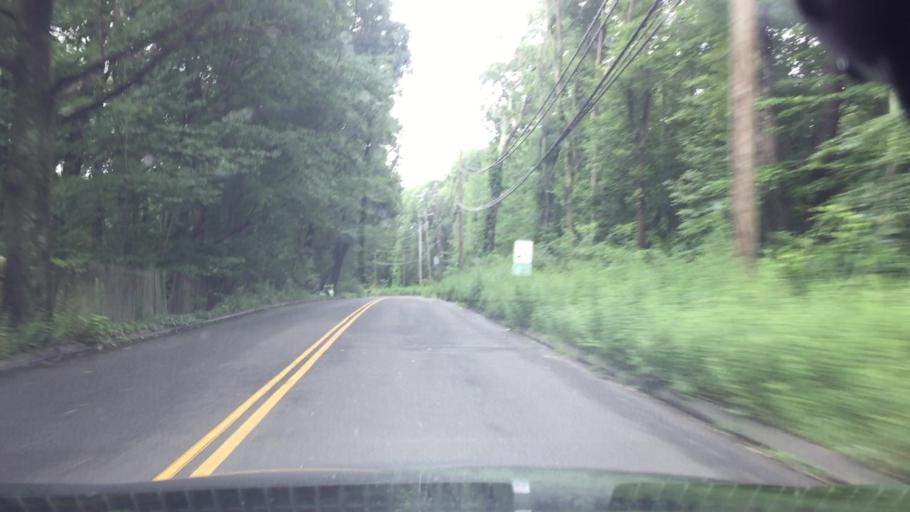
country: US
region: Connecticut
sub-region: Fairfield County
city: Shelton
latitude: 41.2646
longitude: -73.1203
